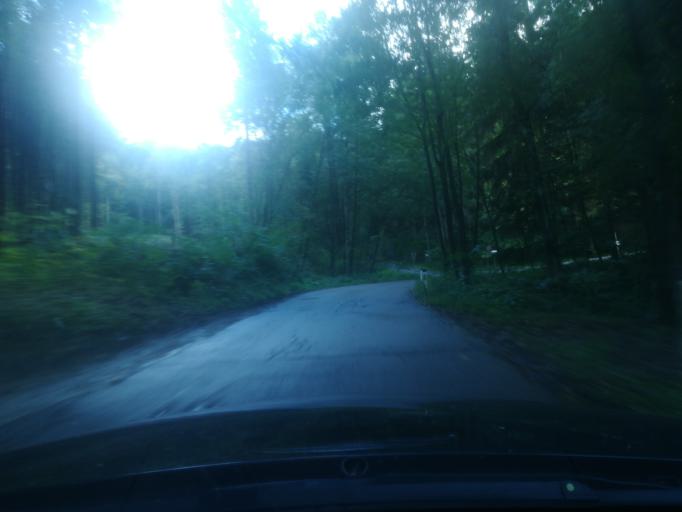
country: AT
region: Upper Austria
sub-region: Linz Stadt
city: Linz
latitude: 48.3432
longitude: 14.2675
